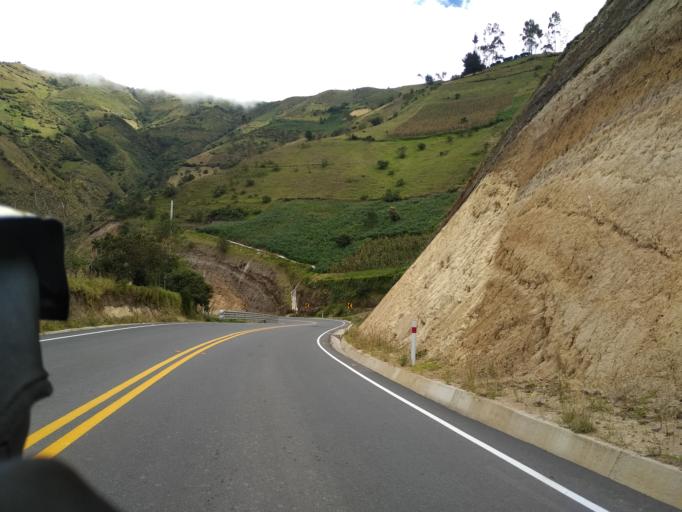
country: EC
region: Cotopaxi
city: Saquisili
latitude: -0.7644
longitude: -78.9114
